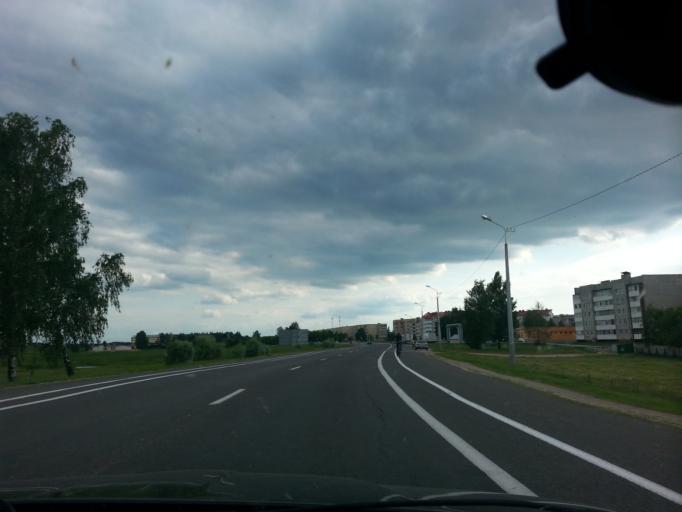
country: BY
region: Minsk
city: Myadzyel
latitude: 54.8745
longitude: 26.9406
